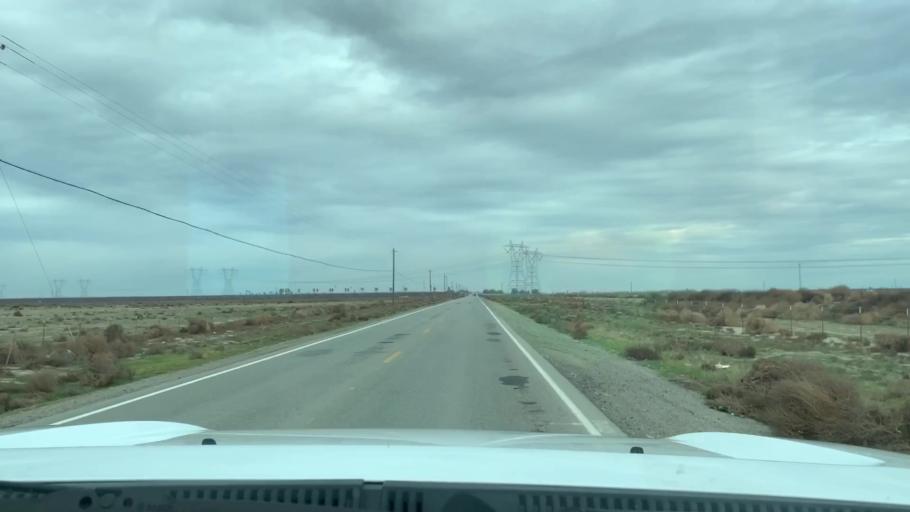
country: US
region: California
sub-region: Kern County
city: Rosedale
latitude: 35.2749
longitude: -119.2526
